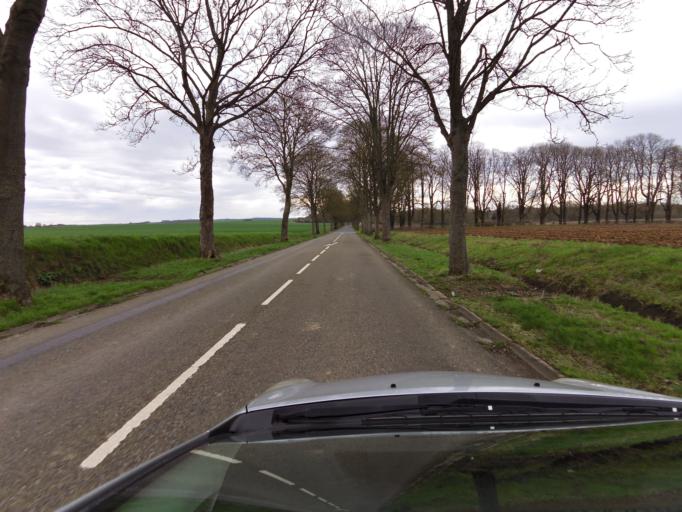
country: FR
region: Picardie
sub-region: Departement de l'Oise
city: Chamant
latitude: 49.1979
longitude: 2.6163
